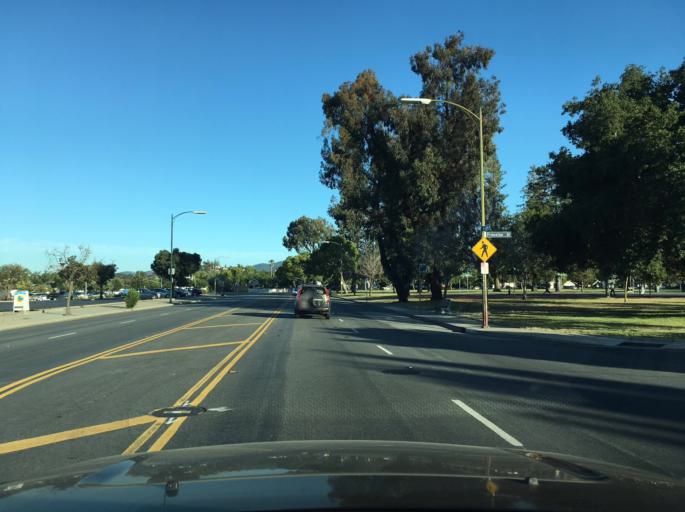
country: US
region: California
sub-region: Santa Clara County
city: Cambrian Park
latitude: 37.2449
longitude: -121.8916
